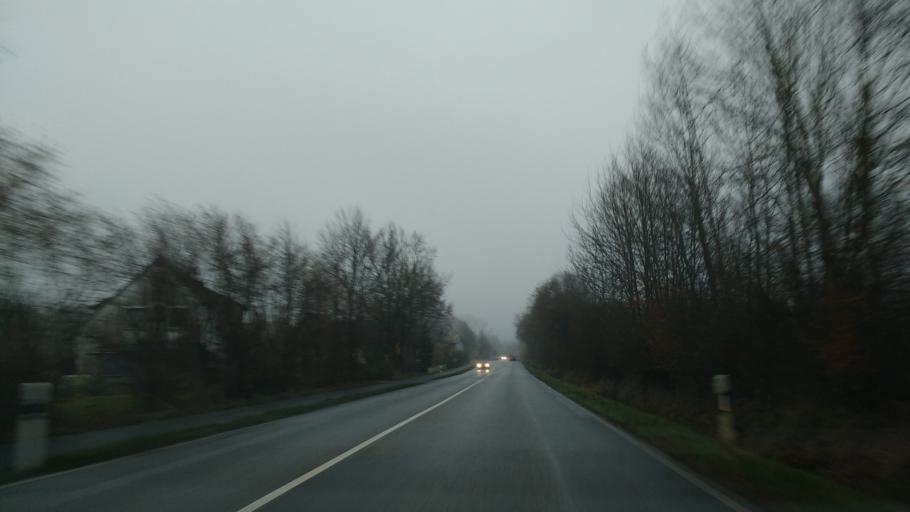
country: DE
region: Schleswig-Holstein
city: Brinjahe
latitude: 54.1812
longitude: 9.6357
